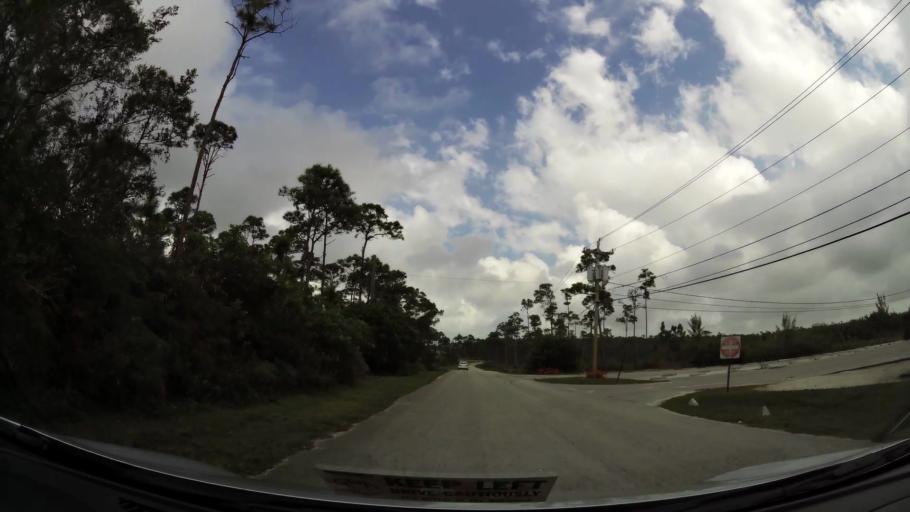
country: BS
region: Freeport
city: Lucaya
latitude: 26.5454
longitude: -78.5949
